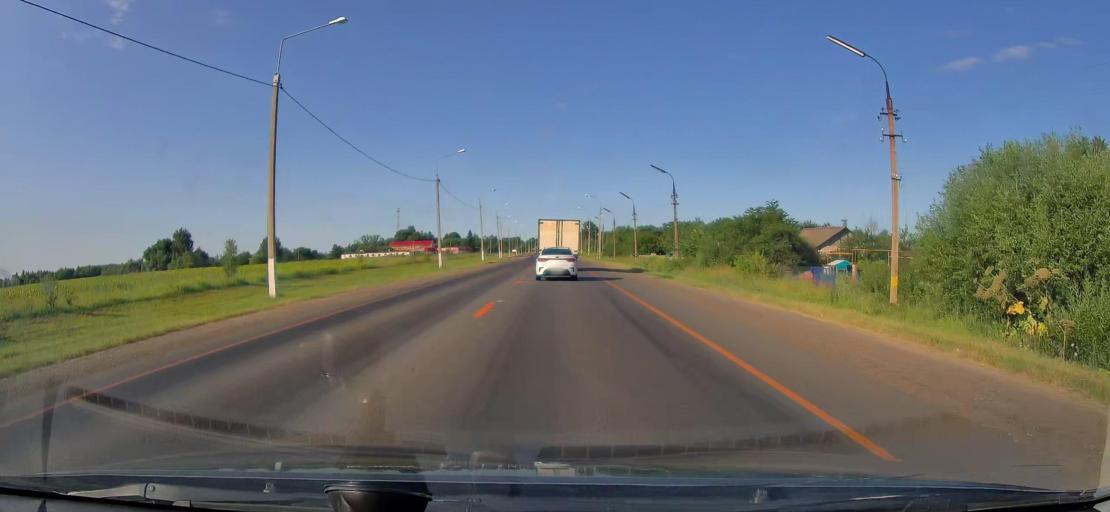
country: RU
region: Tula
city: Bol'shoye Skuratovo
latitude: 53.4003
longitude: 36.7634
